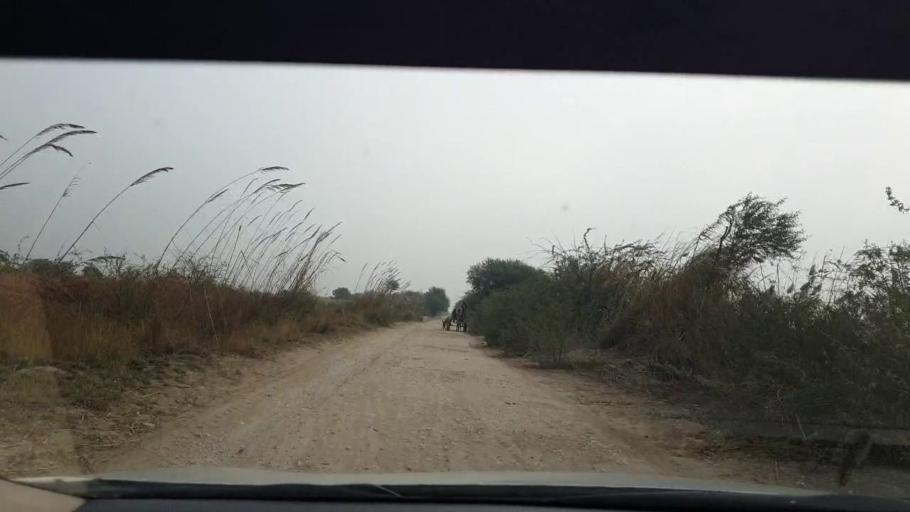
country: PK
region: Sindh
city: Berani
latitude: 25.8636
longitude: 68.8282
